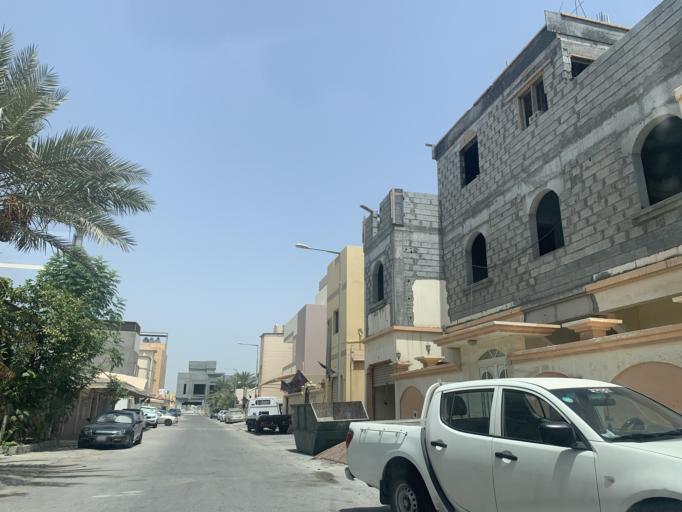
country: BH
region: Central Governorate
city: Madinat Hamad
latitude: 26.1455
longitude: 50.5052
